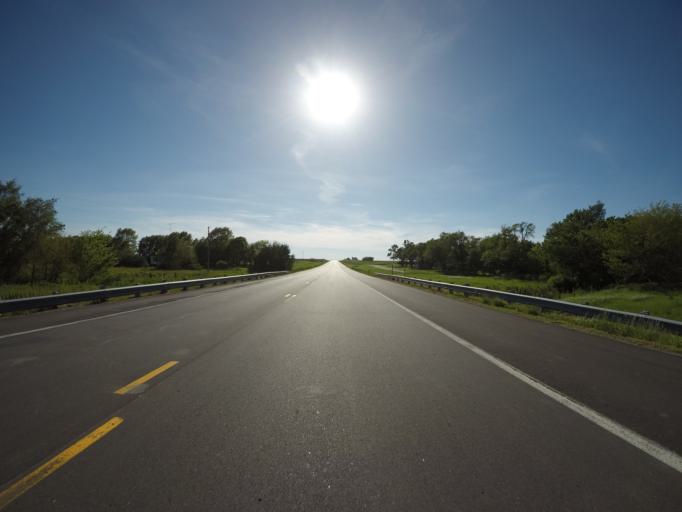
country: US
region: Kansas
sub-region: Clay County
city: Clay Center
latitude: 39.3795
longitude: -96.9878
